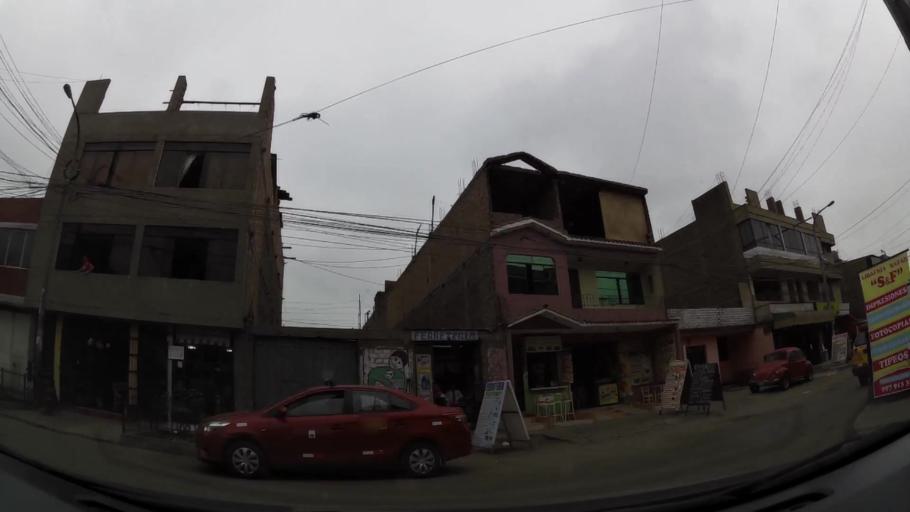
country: PE
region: Lima
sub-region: Lima
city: Independencia
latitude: -11.9729
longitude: -77.0585
